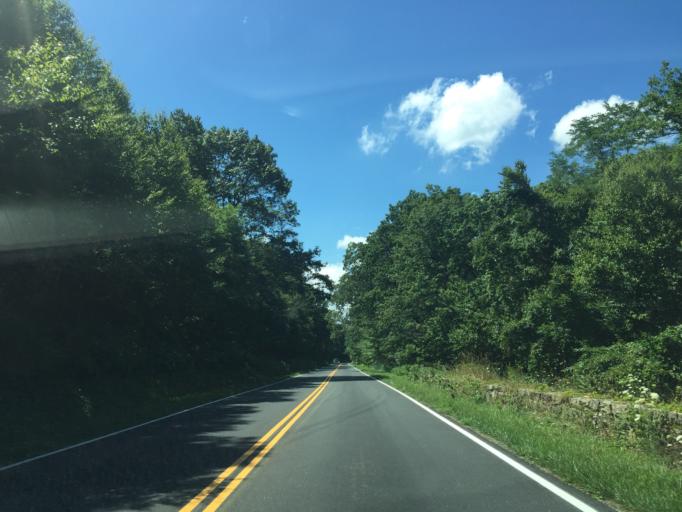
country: US
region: Virginia
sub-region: Rappahannock County
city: Washington
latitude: 38.7533
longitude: -78.2962
